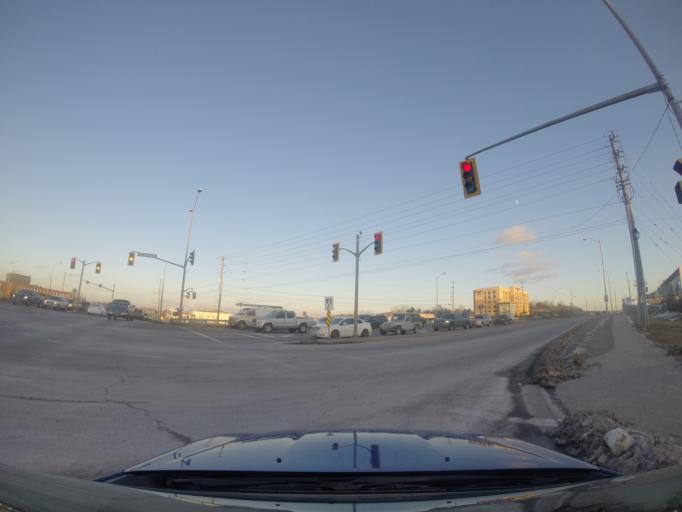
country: CA
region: Ontario
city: Greater Sudbury
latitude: 46.5050
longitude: -80.9381
